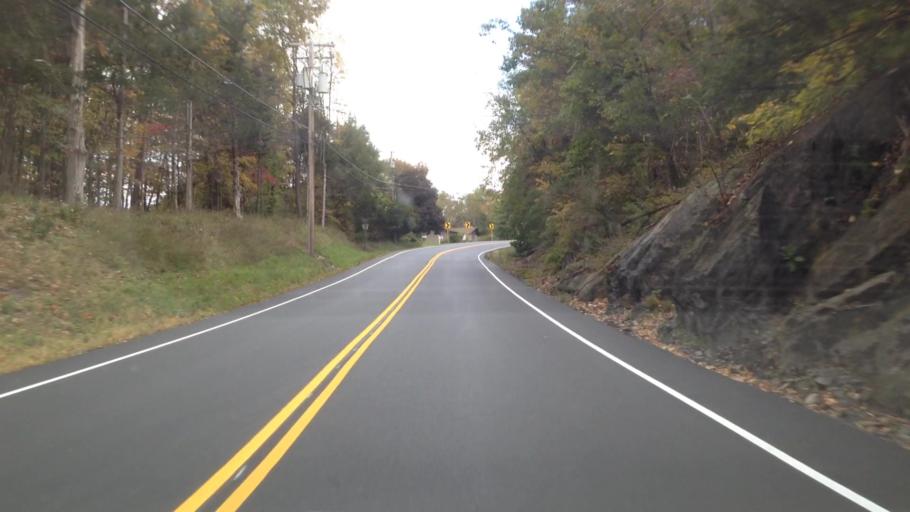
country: US
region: New York
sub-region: Ulster County
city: New Paltz
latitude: 41.7286
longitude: -74.0988
